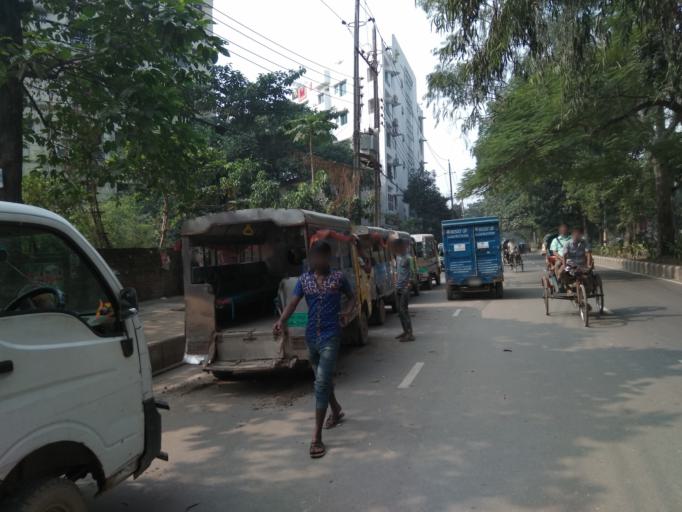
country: BD
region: Dhaka
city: Tungi
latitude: 23.8608
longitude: 90.3982
